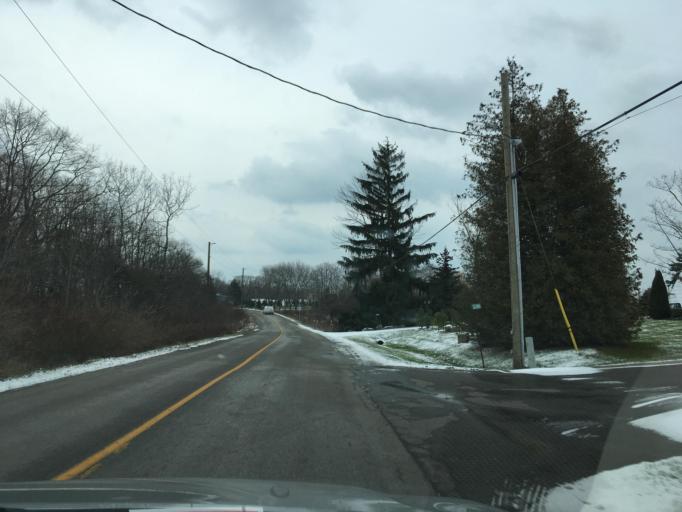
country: CA
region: Ontario
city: Norfolk County
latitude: 42.7875
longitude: -80.1602
